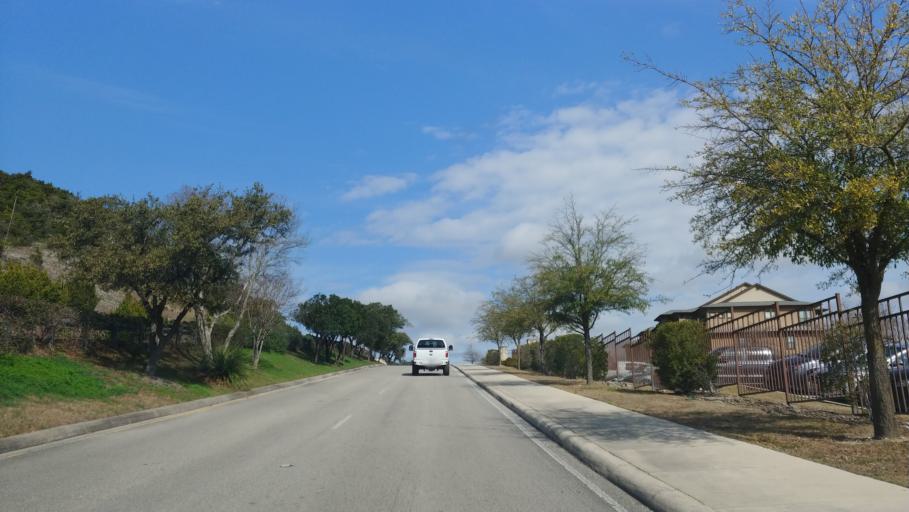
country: US
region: Texas
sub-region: Bexar County
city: Cross Mountain
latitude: 29.6220
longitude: -98.6123
